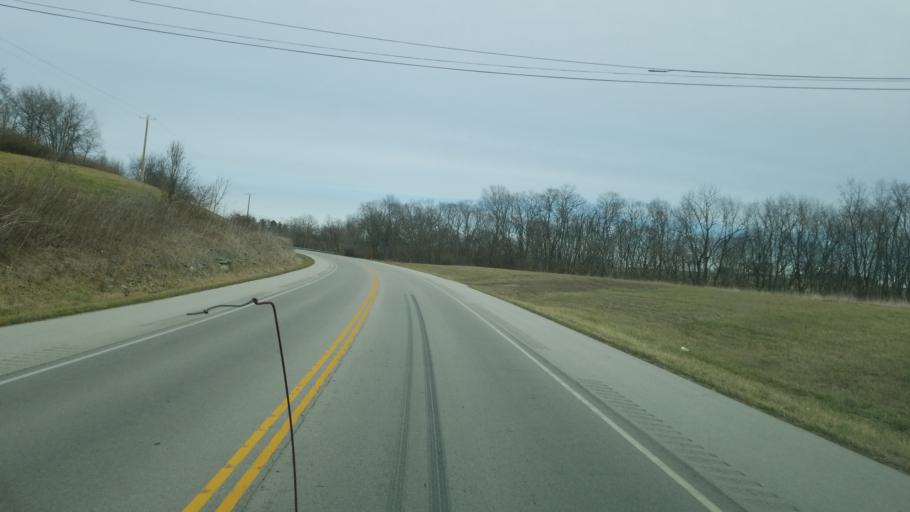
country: US
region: Ohio
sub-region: Brown County
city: Aberdeen
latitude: 38.5956
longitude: -83.8140
